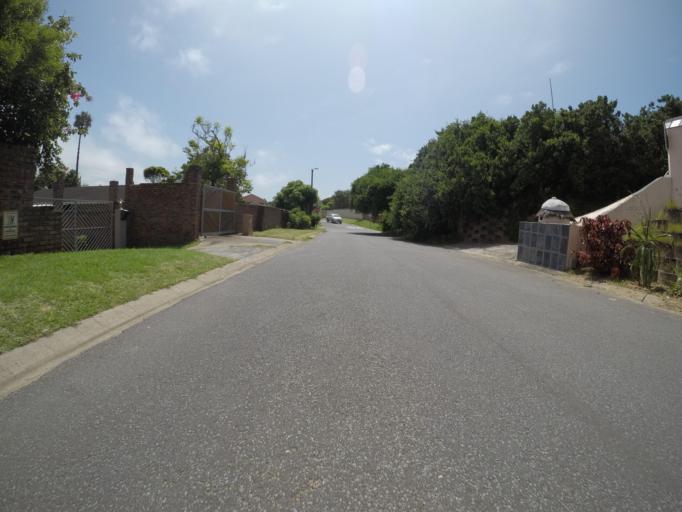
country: ZA
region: Eastern Cape
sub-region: Buffalo City Metropolitan Municipality
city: East London
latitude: -32.9472
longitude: 28.0194
